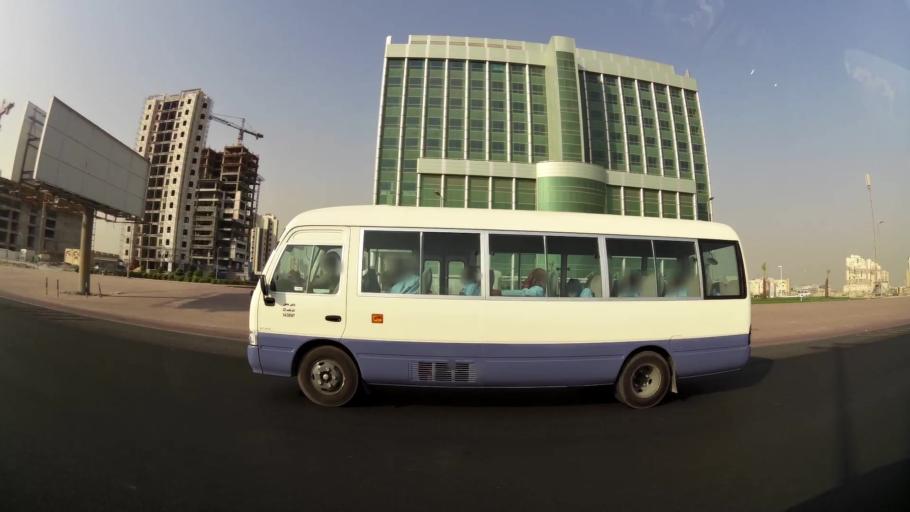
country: KW
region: Mubarak al Kabir
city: Sabah as Salim
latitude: 29.2580
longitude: 48.0884
